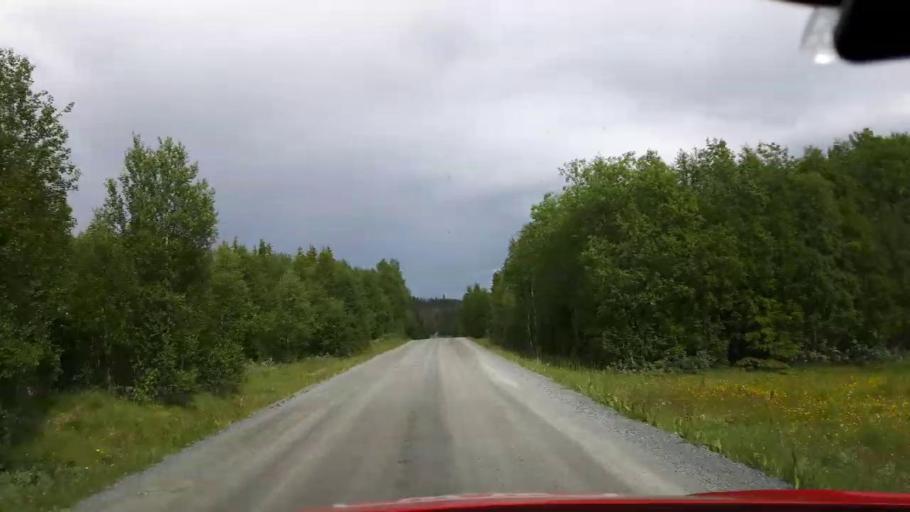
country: NO
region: Nord-Trondelag
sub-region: Lierne
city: Sandvika
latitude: 64.1456
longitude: 13.9440
